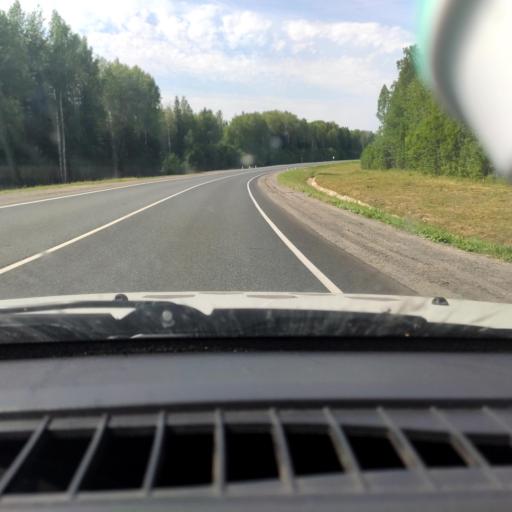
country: RU
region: Kirov
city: Kostino
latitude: 58.7361
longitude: 53.6276
